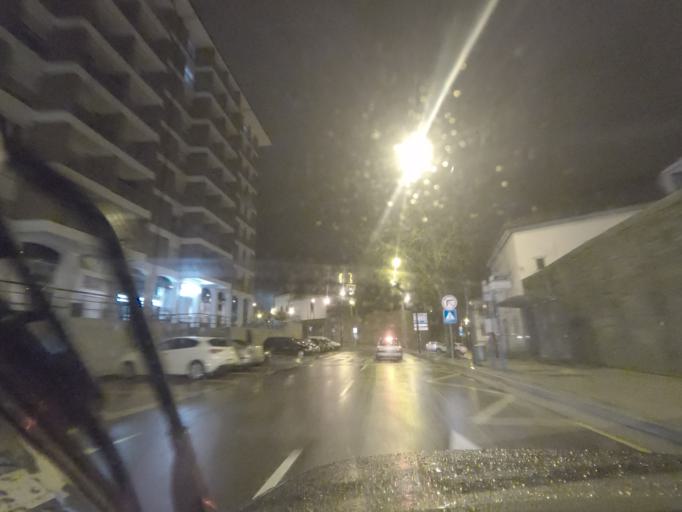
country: PT
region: Vila Real
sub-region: Vila Real
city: Vila Real
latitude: 41.3001
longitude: -7.7439
